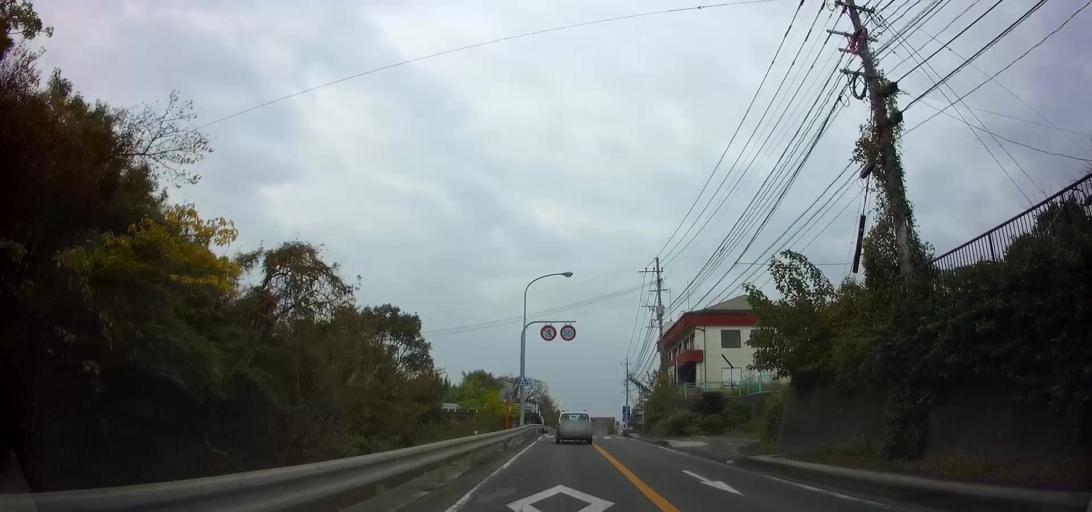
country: JP
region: Nagasaki
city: Shimabara
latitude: 32.6557
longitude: 130.2916
